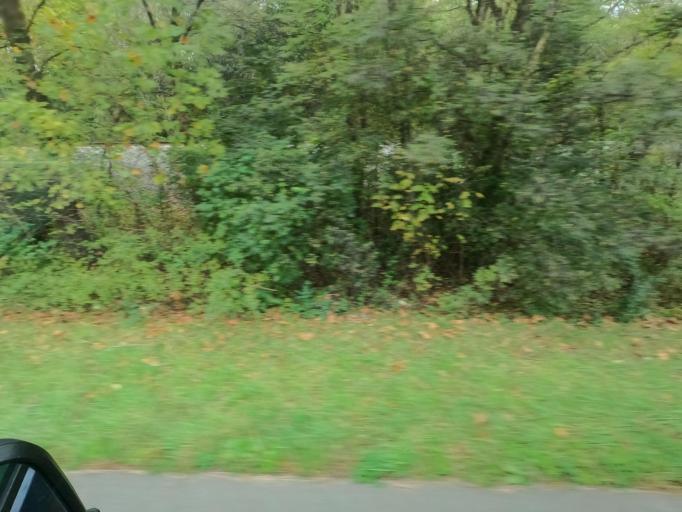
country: US
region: Tennessee
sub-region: Cheatham County
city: Pegram
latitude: 36.0950
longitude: -87.0266
